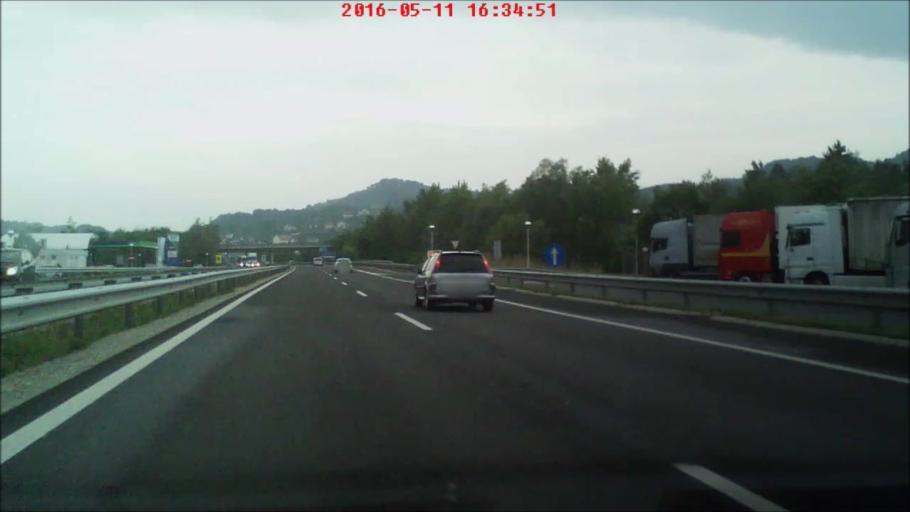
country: SI
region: Pesnica
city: Pesnica pri Mariboru
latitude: 46.6093
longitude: 15.6629
